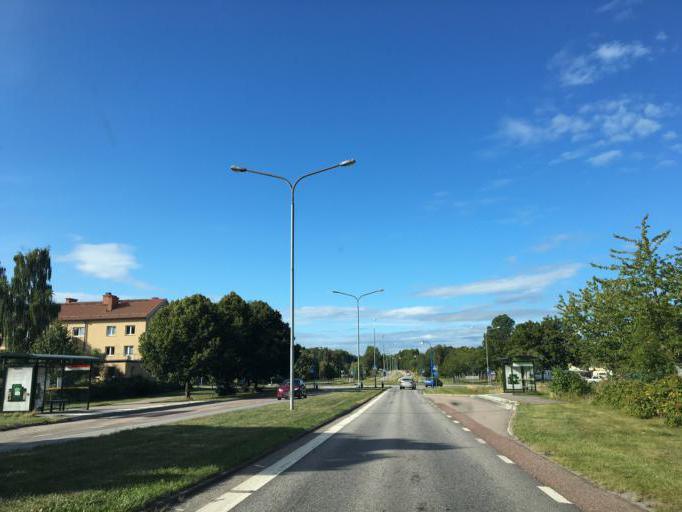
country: SE
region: Soedermanland
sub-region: Nykopings Kommun
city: Nykoping
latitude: 58.7692
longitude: 16.9865
